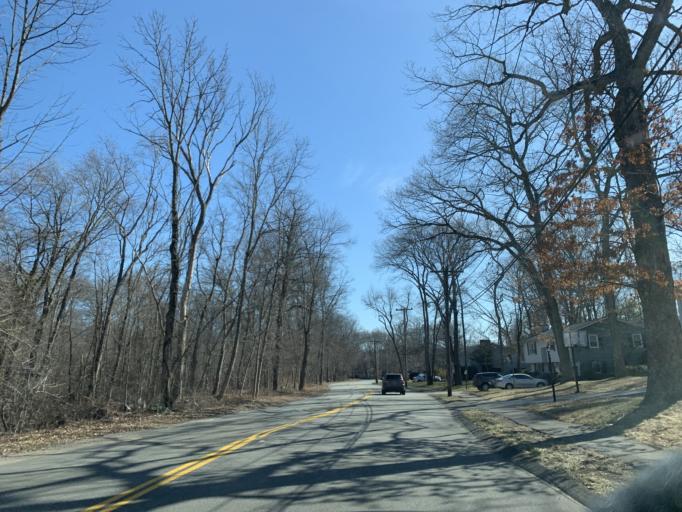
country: US
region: Massachusetts
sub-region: Norfolk County
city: Norwood
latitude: 42.1886
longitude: -71.2238
